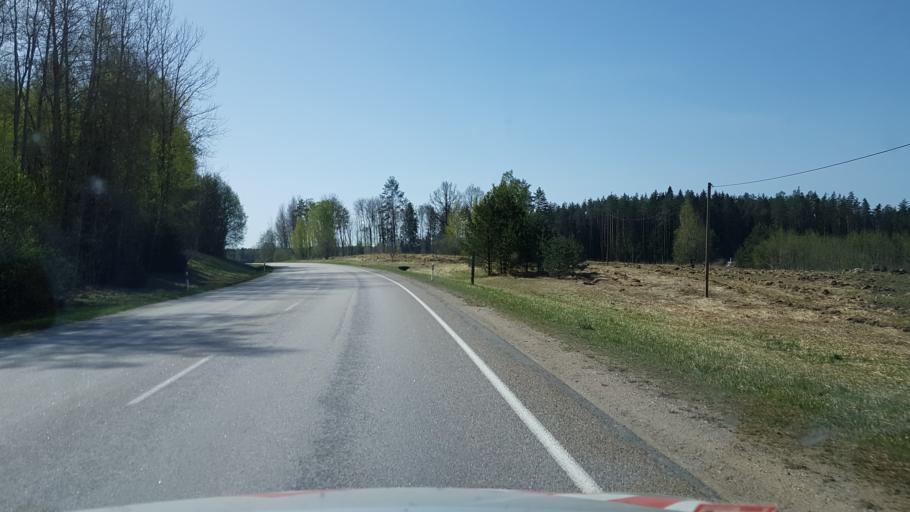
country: EE
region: Valgamaa
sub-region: Valga linn
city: Valga
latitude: 57.8666
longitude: 26.0575
